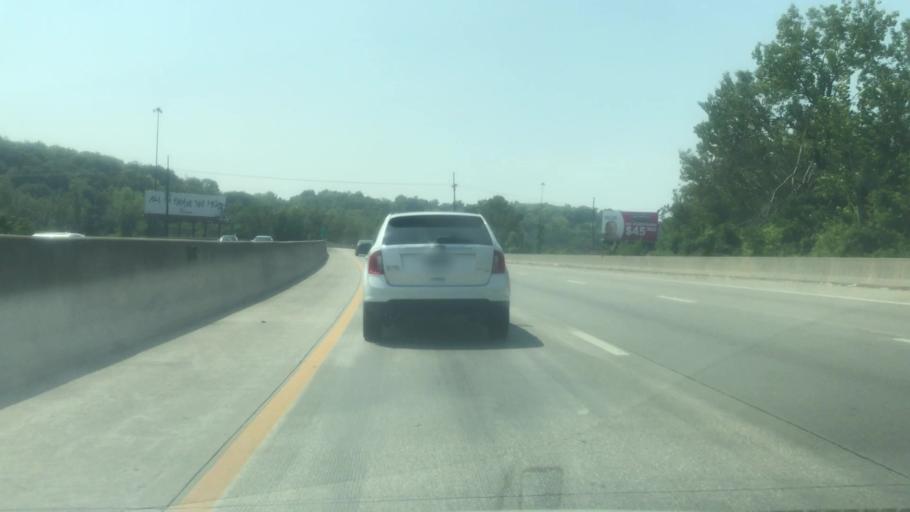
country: US
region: Kansas
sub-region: Johnson County
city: Westwood
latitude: 39.0598
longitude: -94.6279
